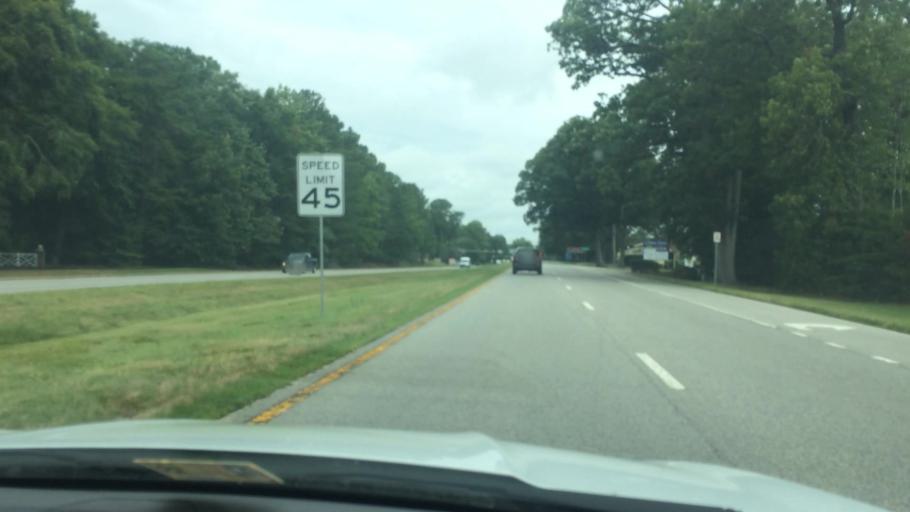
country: US
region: Virginia
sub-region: City of Williamsburg
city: Williamsburg
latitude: 37.2438
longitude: -76.6557
